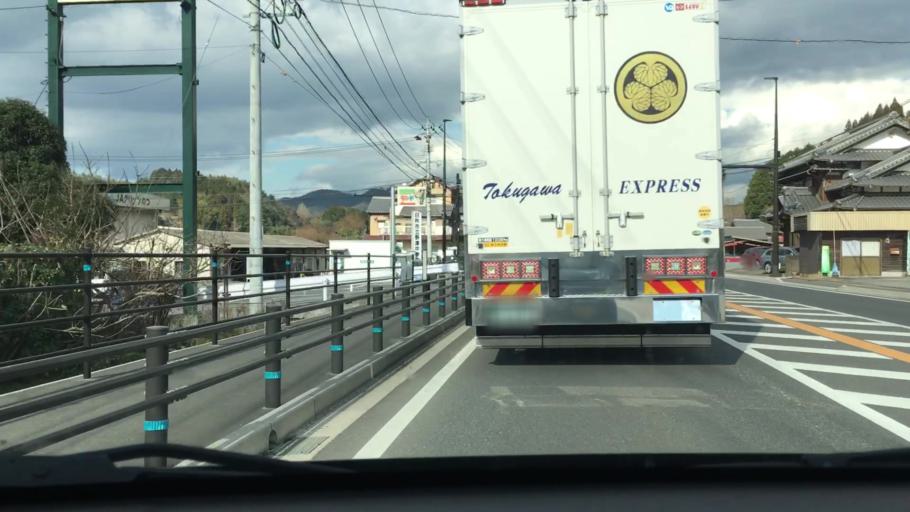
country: JP
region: Oita
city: Usuki
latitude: 33.0374
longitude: 131.6895
